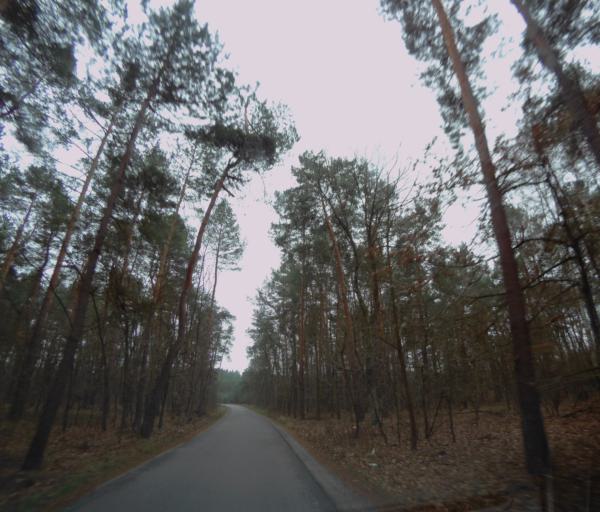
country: PL
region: Subcarpathian Voivodeship
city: Nowa Sarzyna
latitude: 50.3015
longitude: 22.3476
